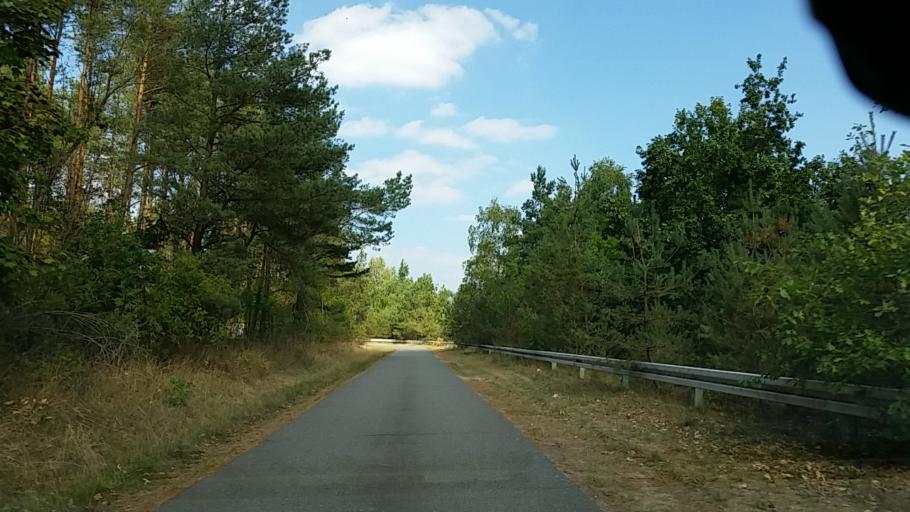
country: DE
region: Lower Saxony
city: Wendisch Evern
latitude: 53.2336
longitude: 10.4880
